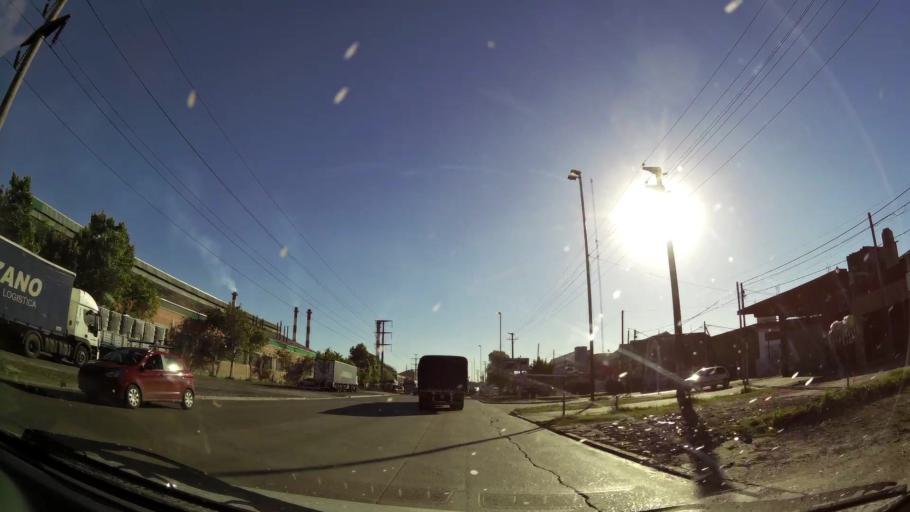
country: AR
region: Buenos Aires
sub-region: Partido de Almirante Brown
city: Adrogue
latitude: -34.7489
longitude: -58.3358
